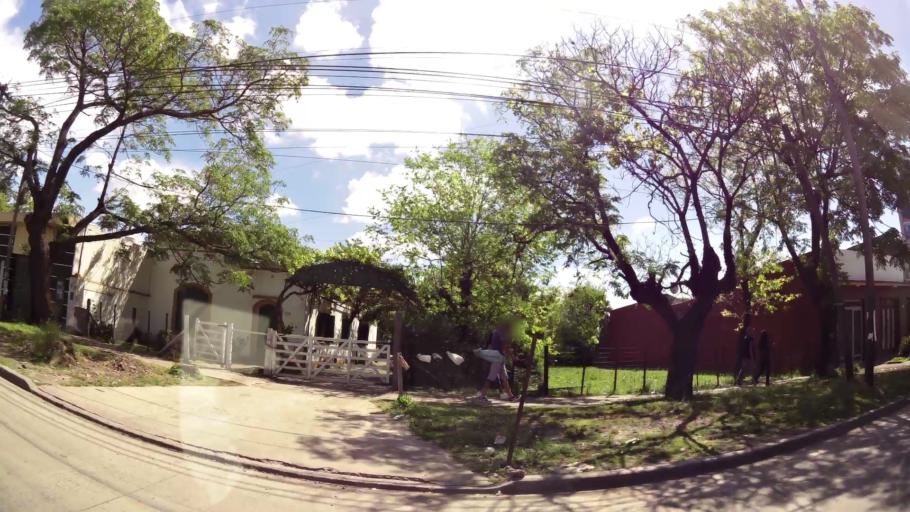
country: AR
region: Buenos Aires
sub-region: Partido de Quilmes
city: Quilmes
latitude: -34.8135
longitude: -58.2777
